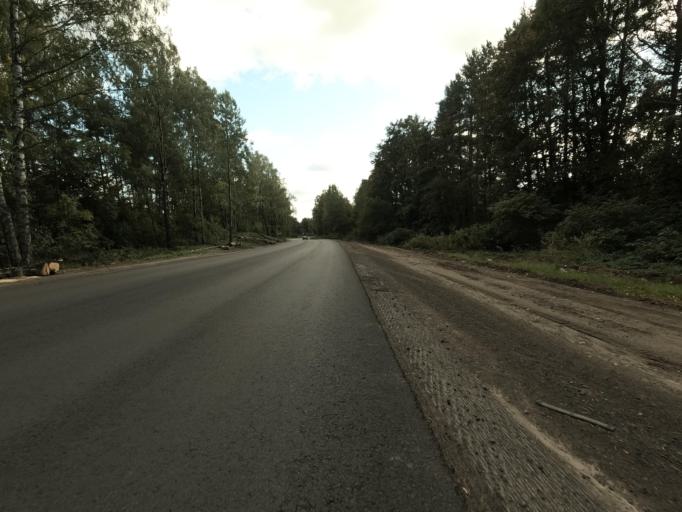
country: RU
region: Leningrad
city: Koltushi
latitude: 59.9498
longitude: 30.6571
